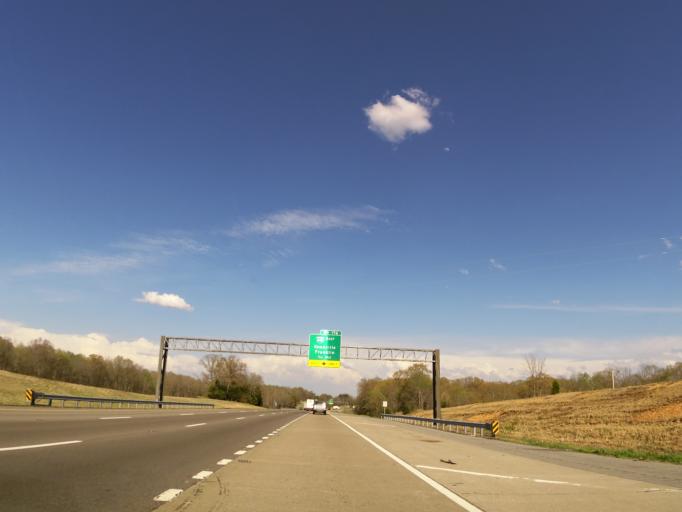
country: US
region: Tennessee
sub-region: Dickson County
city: Burns
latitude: 36.0239
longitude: -87.2865
